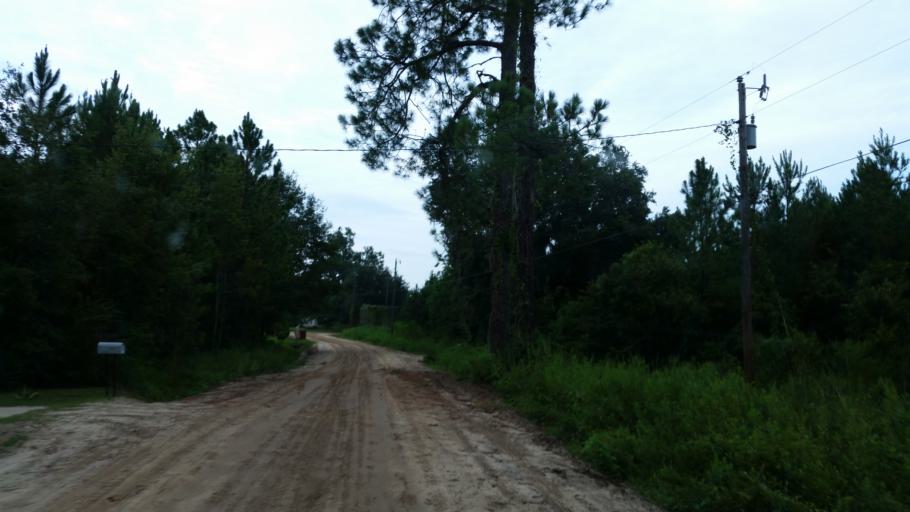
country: US
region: Georgia
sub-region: Lowndes County
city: Valdosta
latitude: 30.7265
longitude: -83.2836
